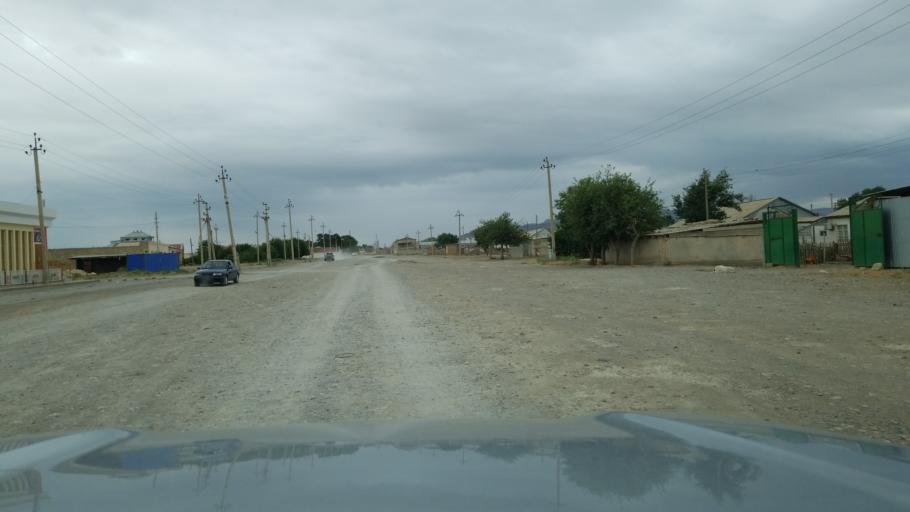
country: TM
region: Balkan
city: Serdar
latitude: 38.9865
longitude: 56.2538
